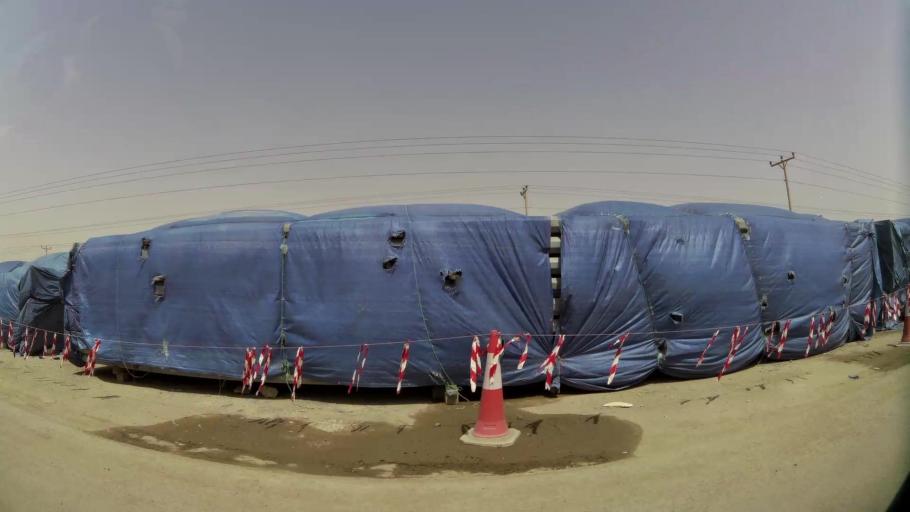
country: QA
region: Baladiyat ar Rayyan
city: Ar Rayyan
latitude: 25.1800
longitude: 51.4207
